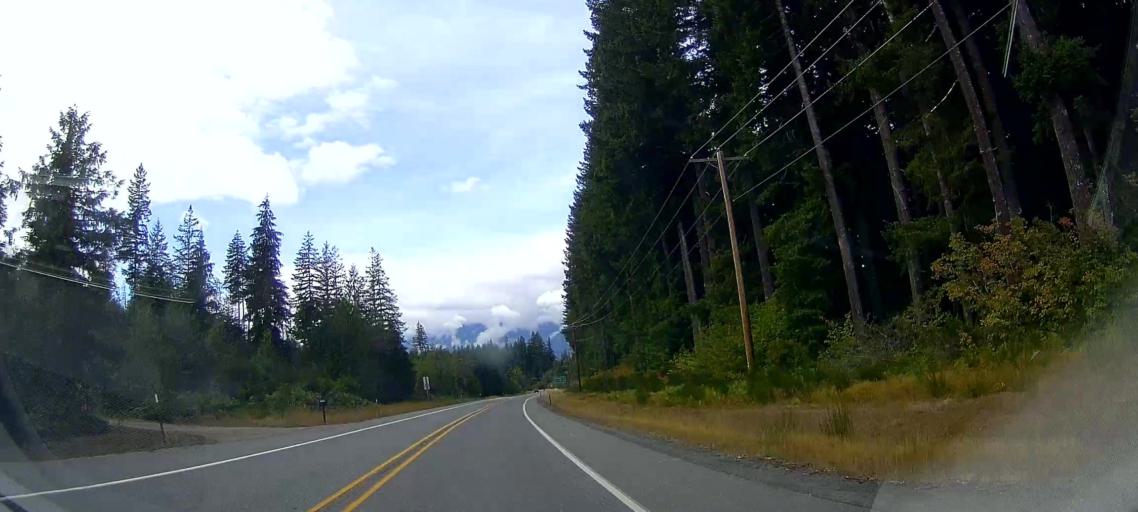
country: US
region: Washington
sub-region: Snohomish County
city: Darrington
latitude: 48.2588
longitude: -121.6174
